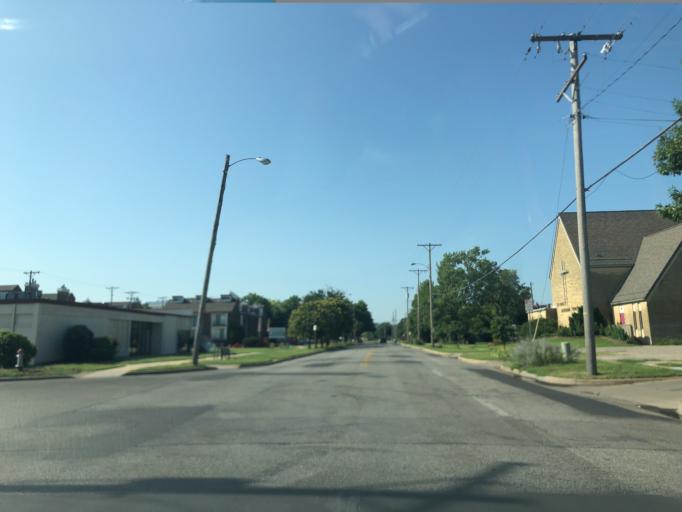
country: US
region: Kansas
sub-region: Sedgwick County
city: Wichita
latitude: 37.7007
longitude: -97.3420
